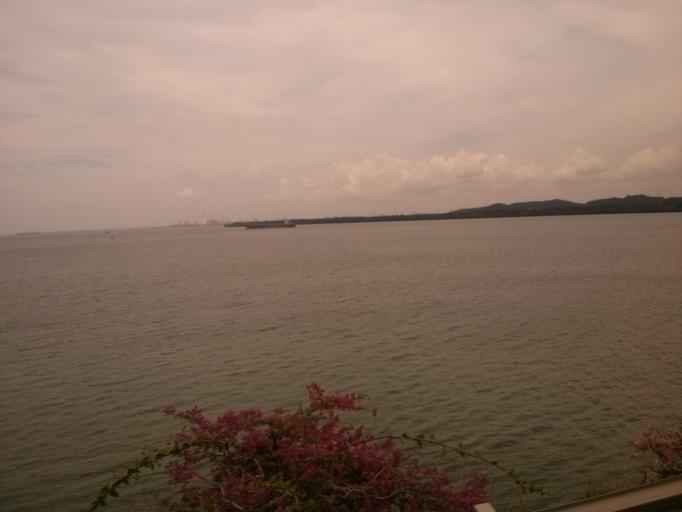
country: MY
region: Johor
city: Johor Bahru
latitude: 1.3493
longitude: 103.6345
